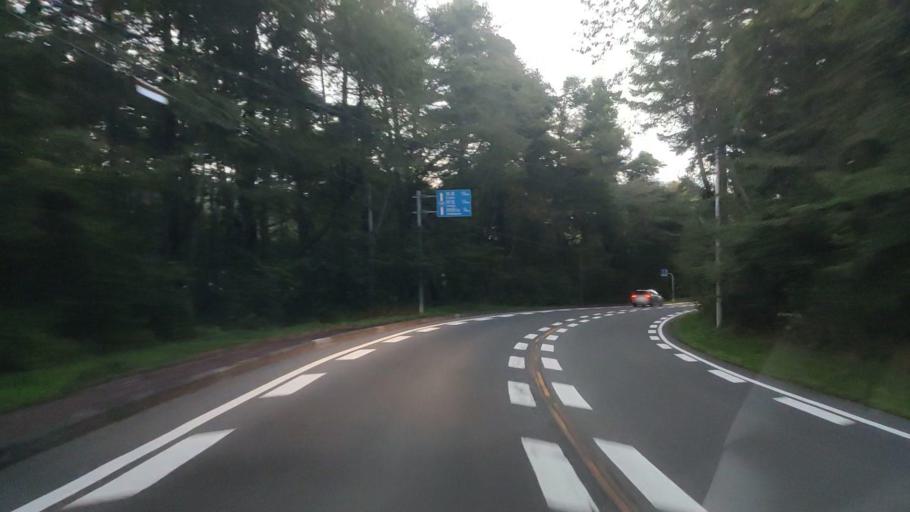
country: JP
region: Gunma
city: Nakanojomachi
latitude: 36.5255
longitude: 138.5997
